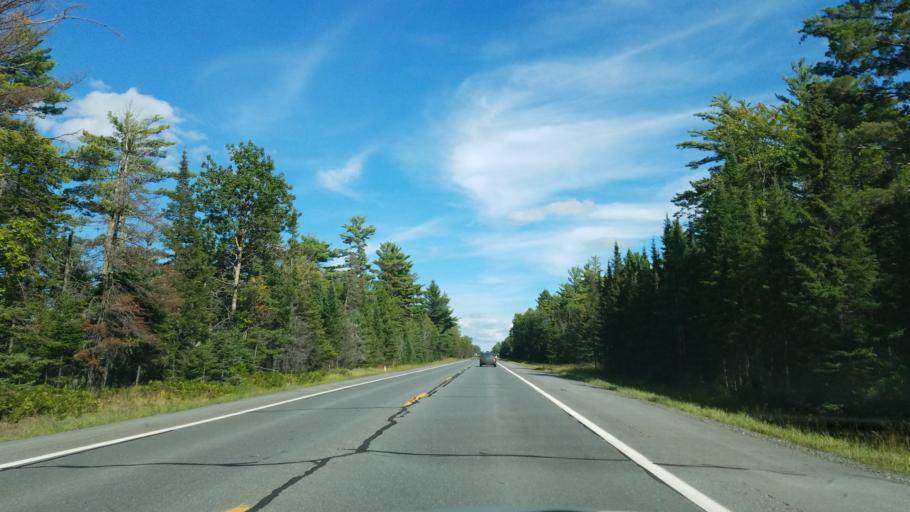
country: US
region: Michigan
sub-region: Baraga County
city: L'Anse
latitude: 46.5788
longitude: -88.4059
